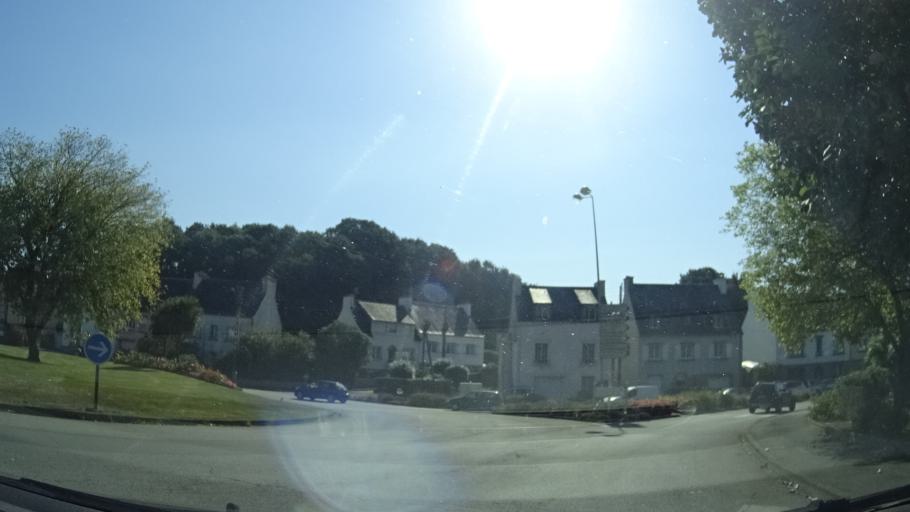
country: FR
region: Brittany
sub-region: Departement du Finistere
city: Douarnenez
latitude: 48.0807
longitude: -4.3272
